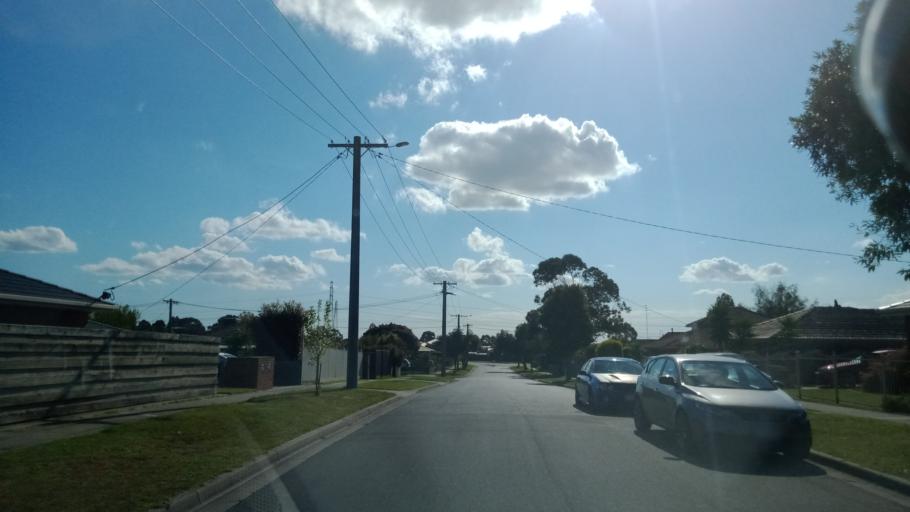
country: AU
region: Victoria
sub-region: Casey
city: Cranbourne West
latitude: -38.1070
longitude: 145.2677
